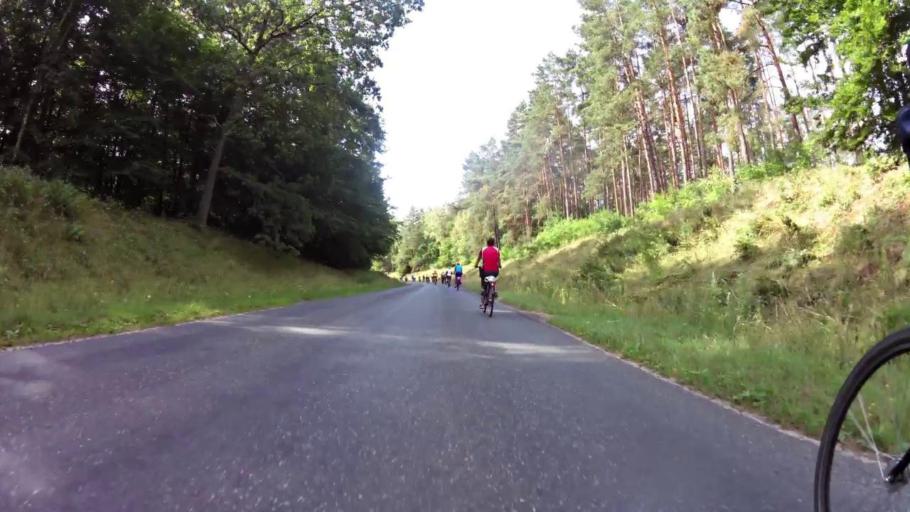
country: PL
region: West Pomeranian Voivodeship
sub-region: Powiat drawski
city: Drawsko Pomorskie
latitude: 53.4825
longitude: 15.7764
